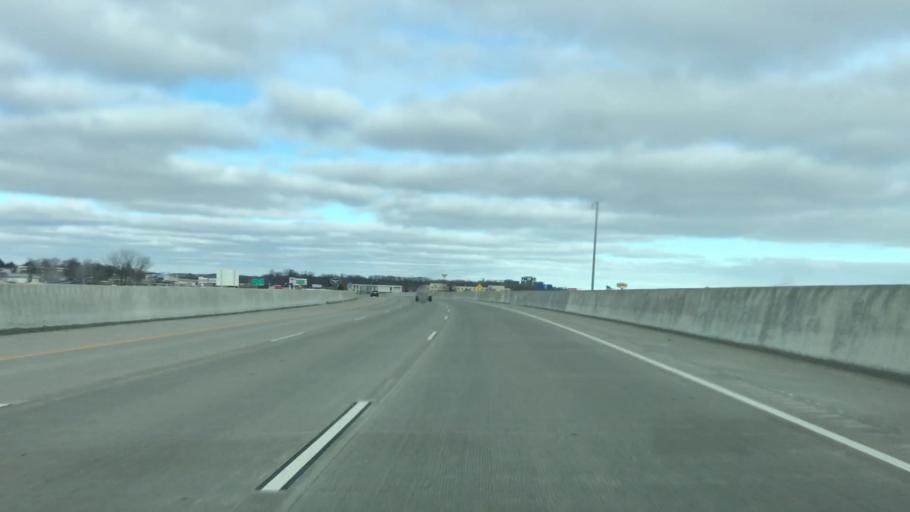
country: US
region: Wisconsin
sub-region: Brown County
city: Ashwaubenon
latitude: 44.4672
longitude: -88.0799
